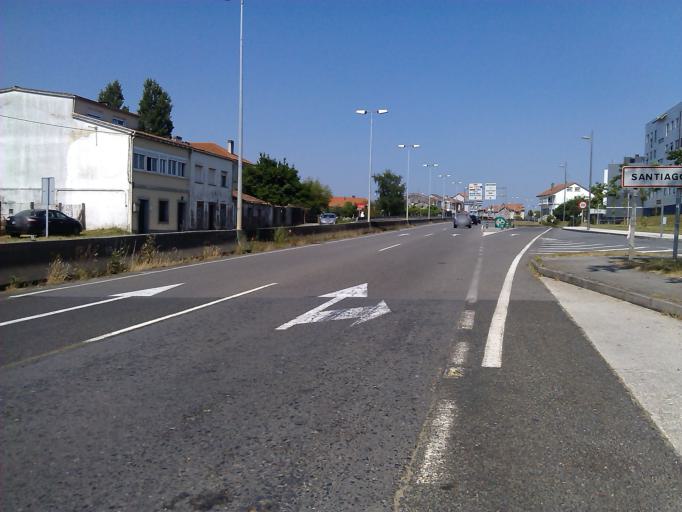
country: ES
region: Galicia
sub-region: Provincia da Coruna
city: Santiago de Compostela
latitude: 42.8580
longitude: -8.5351
